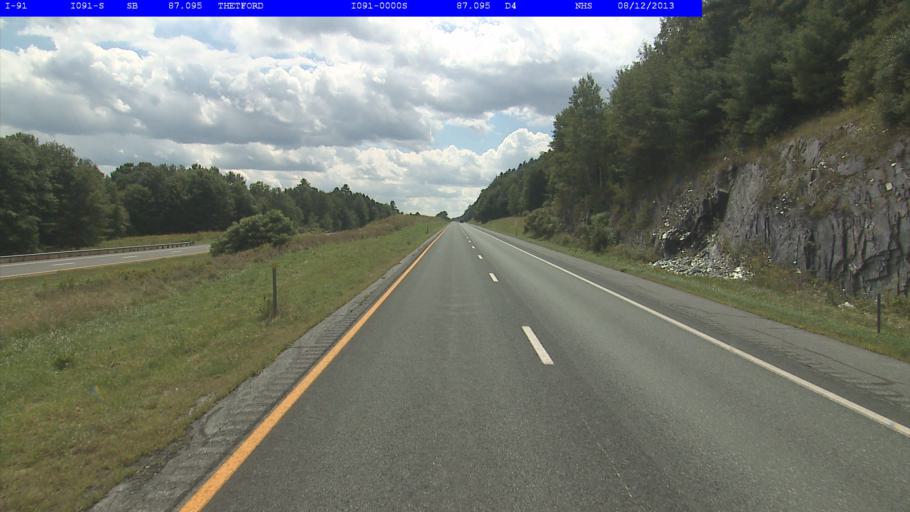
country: US
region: New Hampshire
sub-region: Grafton County
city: Lyme
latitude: 43.8515
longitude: -72.1956
